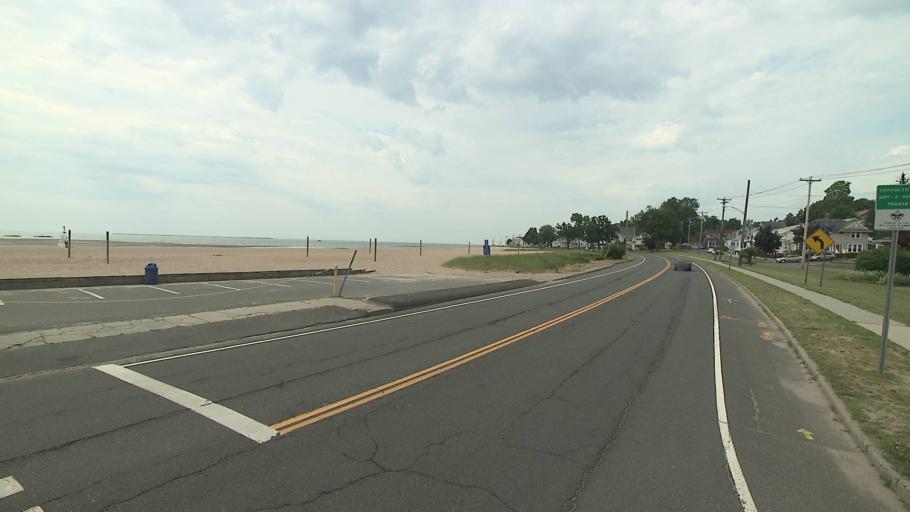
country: US
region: Connecticut
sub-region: New Haven County
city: West Haven
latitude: 41.2525
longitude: -72.9617
